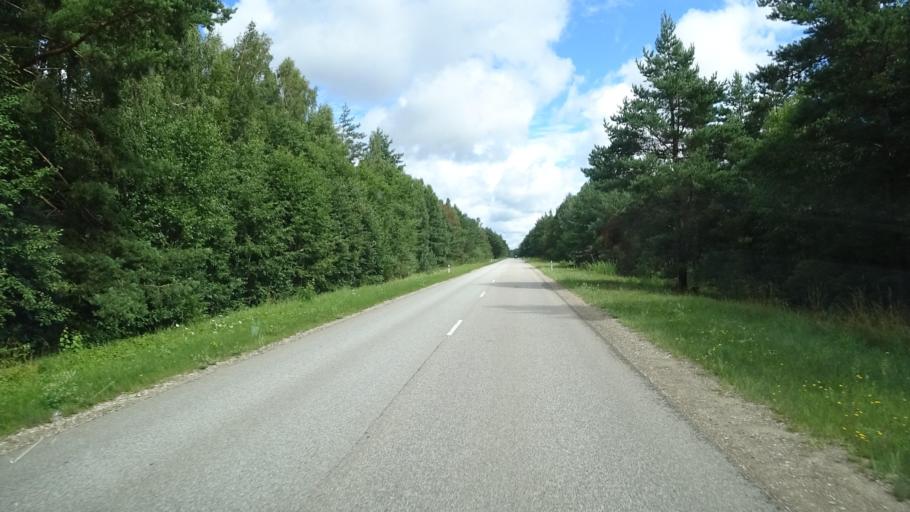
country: LV
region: Grobina
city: Grobina
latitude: 56.6826
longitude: 21.1453
